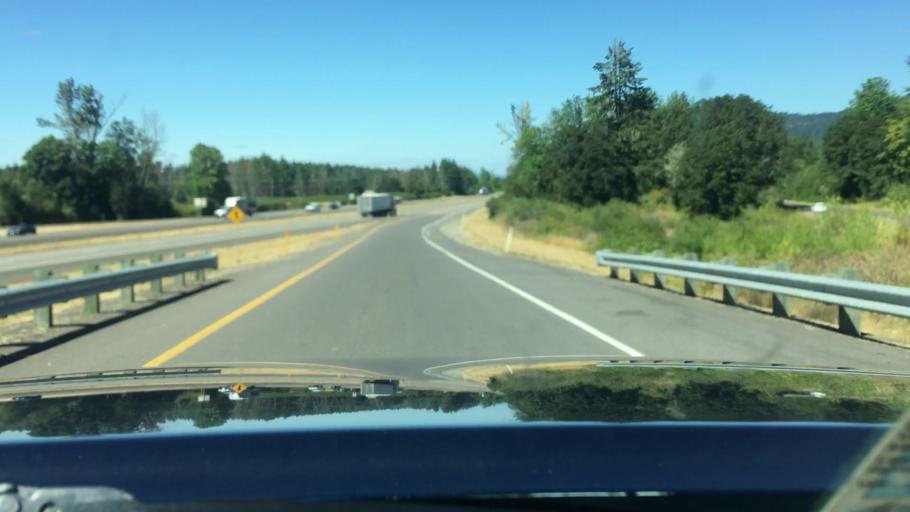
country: US
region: Oregon
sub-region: Lane County
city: Cottage Grove
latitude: 43.8328
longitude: -123.0288
